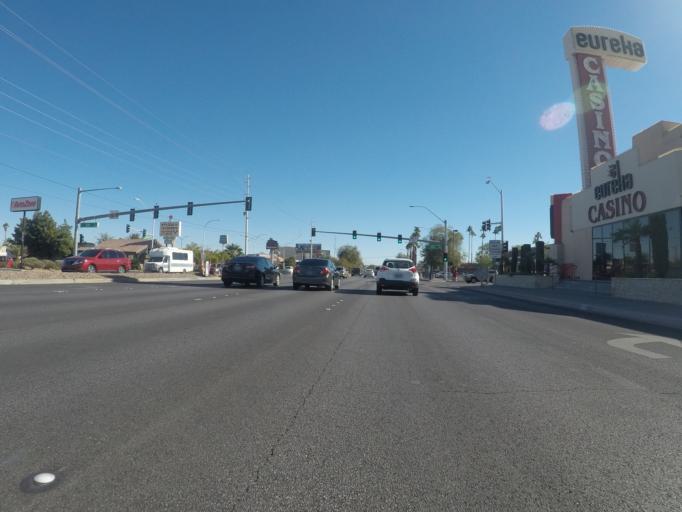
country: US
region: Nevada
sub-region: Clark County
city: Winchester
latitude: 36.1438
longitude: -115.1472
